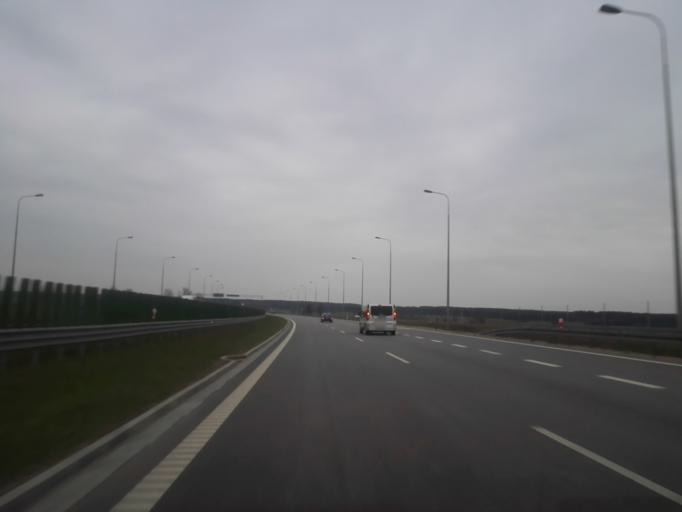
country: PL
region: Podlasie
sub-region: Powiat kolnenski
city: Stawiski
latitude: 53.3860
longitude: 22.1439
